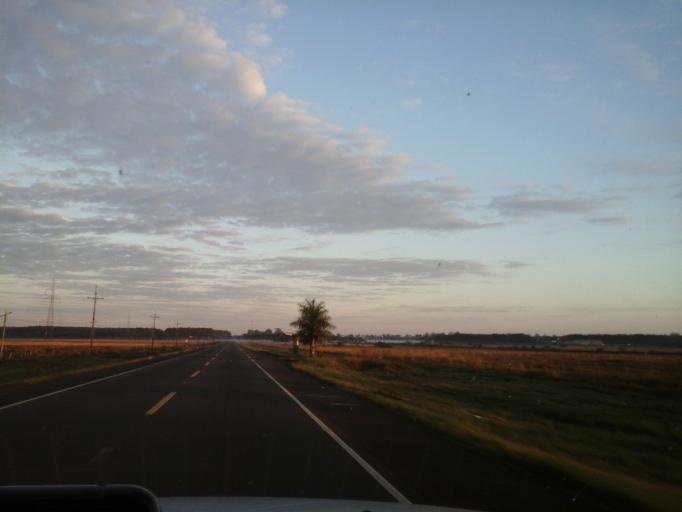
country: PY
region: Itapua
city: General Delgado
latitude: -27.0682
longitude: -56.6127
